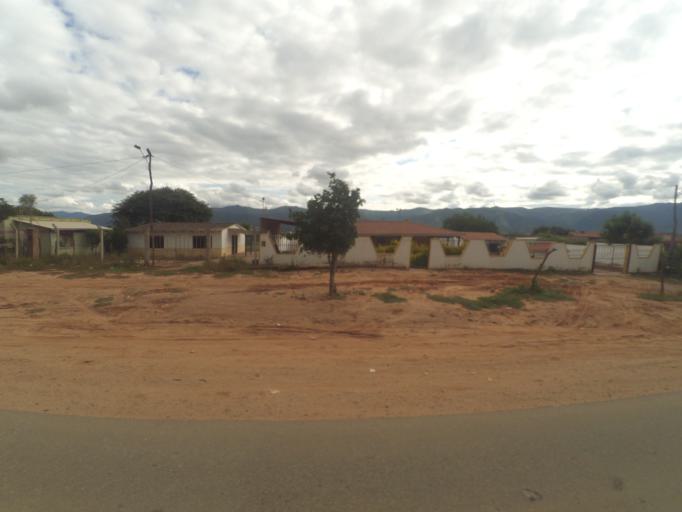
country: BO
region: Santa Cruz
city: Samaipata
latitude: -18.1674
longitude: -63.9098
